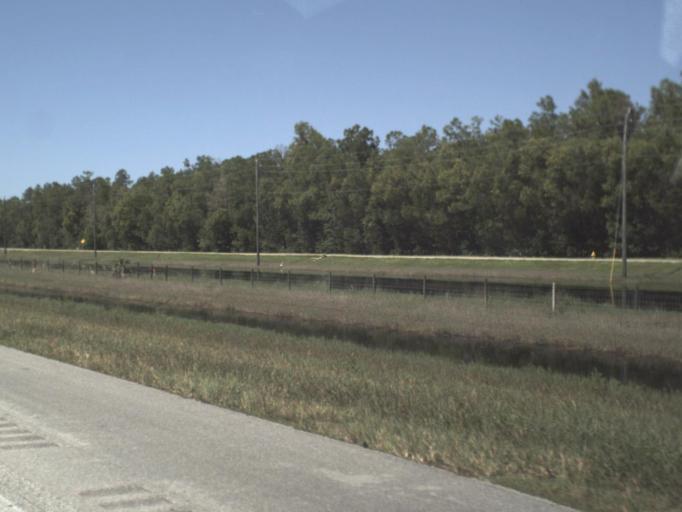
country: US
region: Florida
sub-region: Collier County
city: Golden Gate
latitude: 26.1556
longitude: -81.6671
